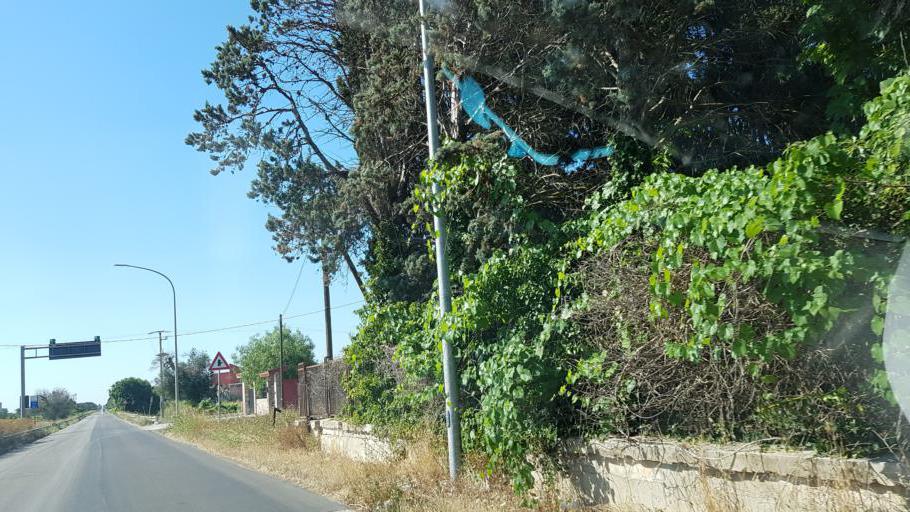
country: IT
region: Apulia
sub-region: Provincia di Brindisi
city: San Donaci
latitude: 40.4547
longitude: 17.9159
